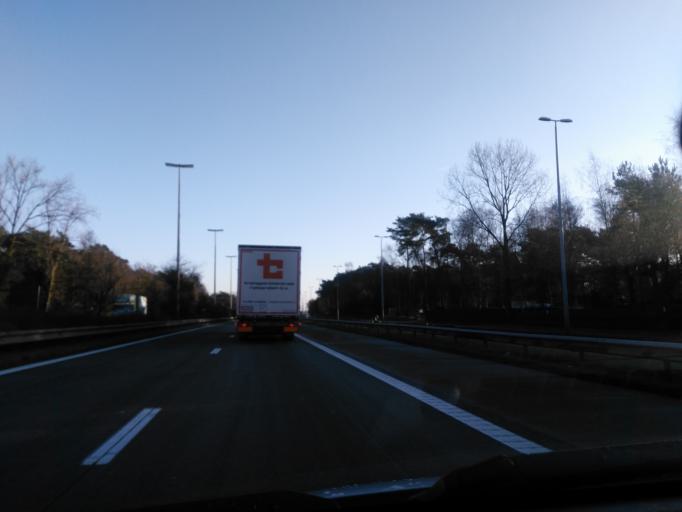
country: BE
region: Flanders
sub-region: Provincie Oost-Vlaanderen
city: Stekene
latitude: 51.2295
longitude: 4.0757
